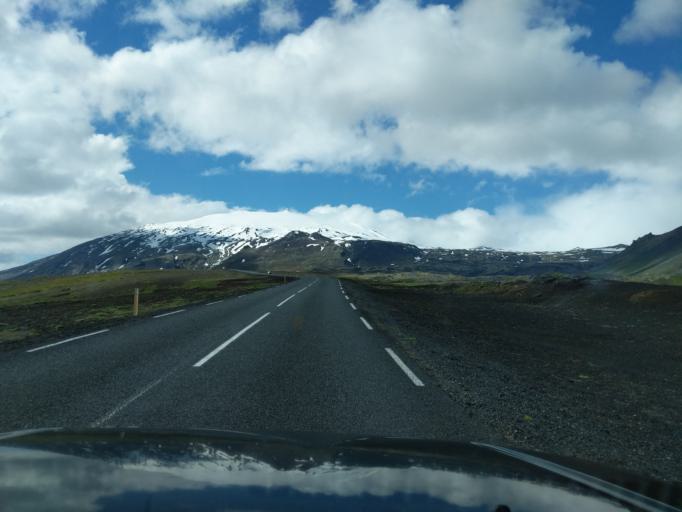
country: IS
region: West
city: Olafsvik
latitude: 64.7512
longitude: -23.6588
